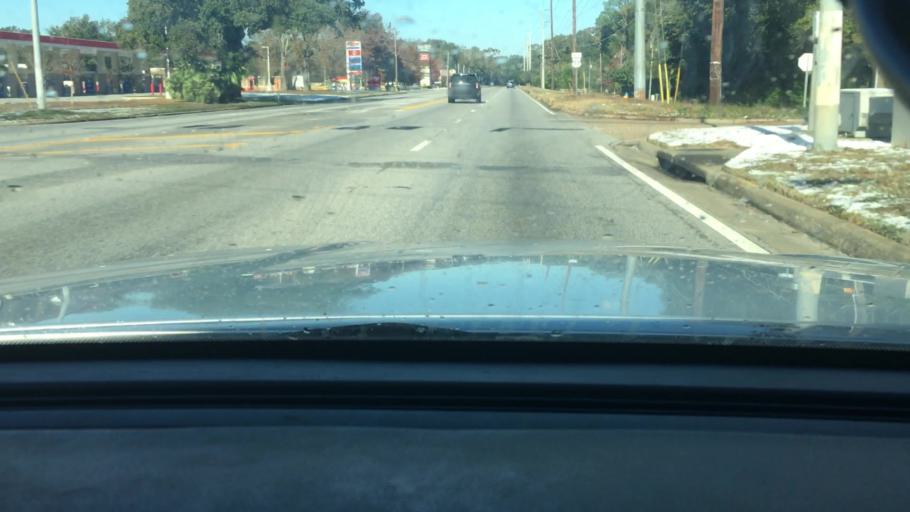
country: US
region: Alabama
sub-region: Mobile County
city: Prichard
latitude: 30.7272
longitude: -88.1703
